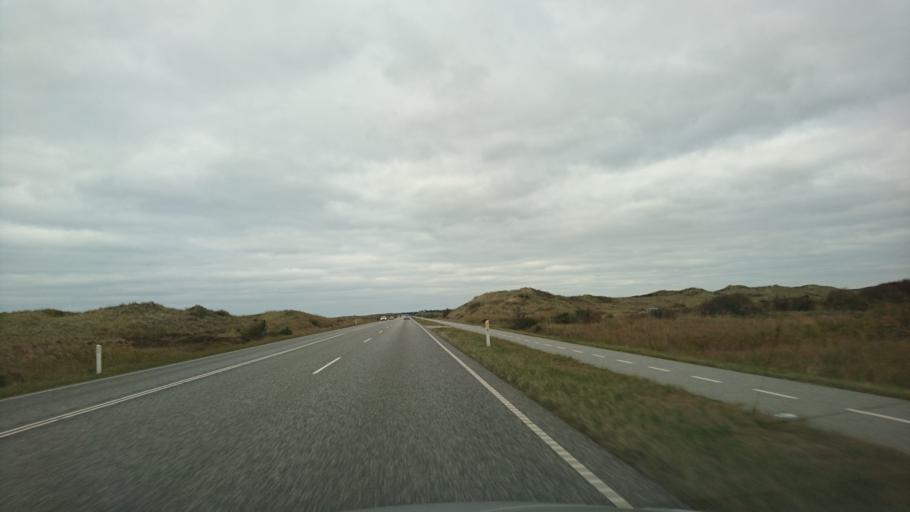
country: DK
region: North Denmark
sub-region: Frederikshavn Kommune
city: Skagen
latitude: 57.6816
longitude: 10.4636
